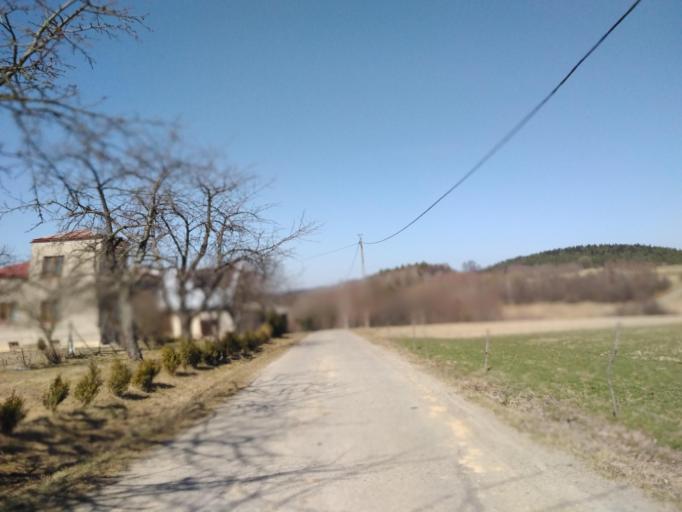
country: PL
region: Subcarpathian Voivodeship
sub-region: Powiat brzozowski
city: Jablonica Polska
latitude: 49.7395
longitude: 21.8952
